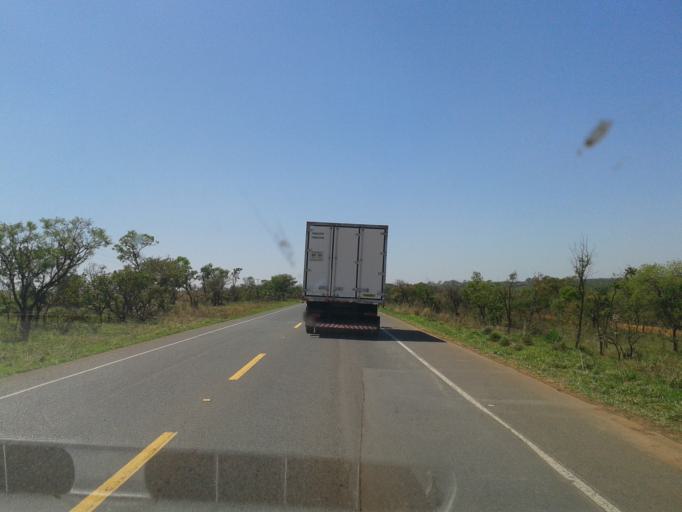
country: BR
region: Minas Gerais
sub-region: Patrocinio
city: Patrocinio
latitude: -19.2820
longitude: -47.4216
